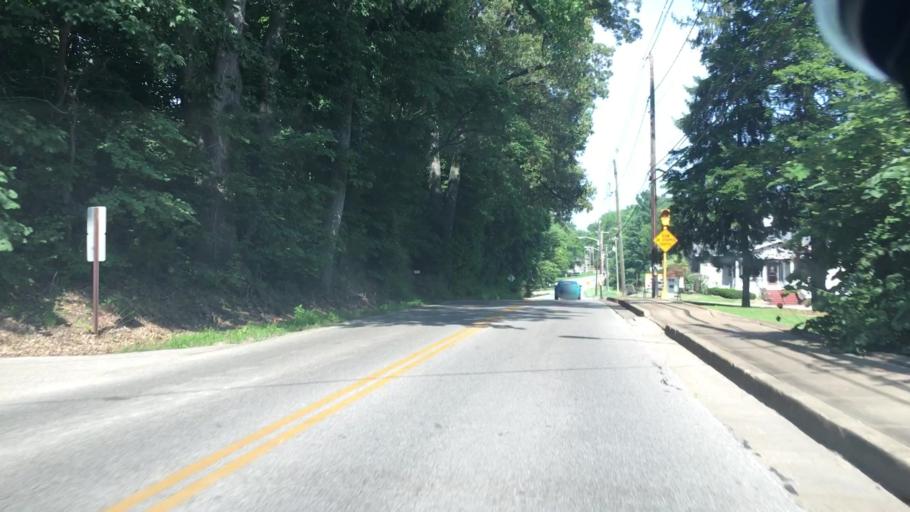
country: US
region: Indiana
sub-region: Vanderburgh County
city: Melody Hill
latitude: 37.9695
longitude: -87.4883
